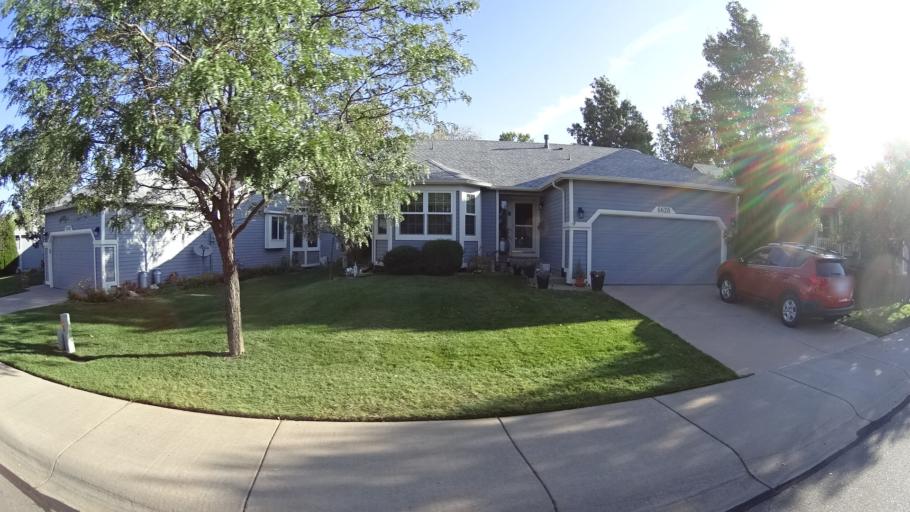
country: US
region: Colorado
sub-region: El Paso County
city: Cimarron Hills
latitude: 38.8895
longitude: -104.7069
